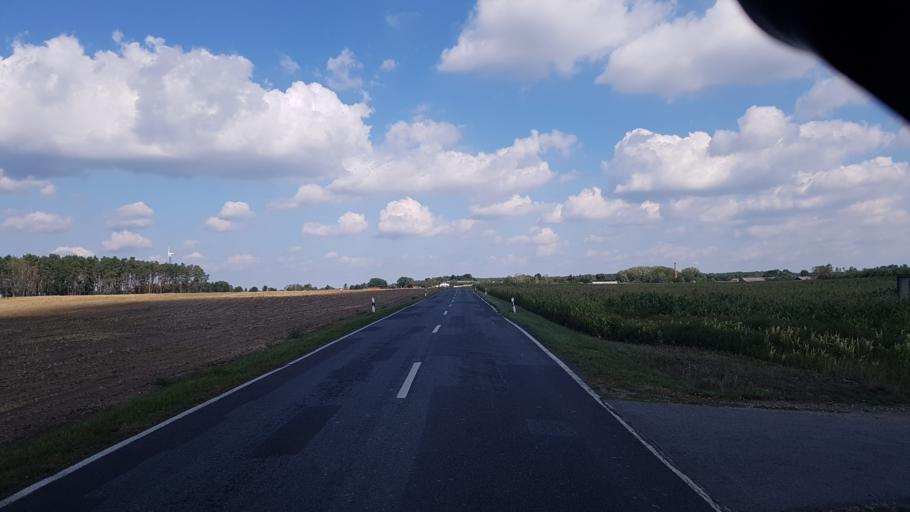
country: DE
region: Brandenburg
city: Drebkau
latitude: 51.6580
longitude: 14.2817
